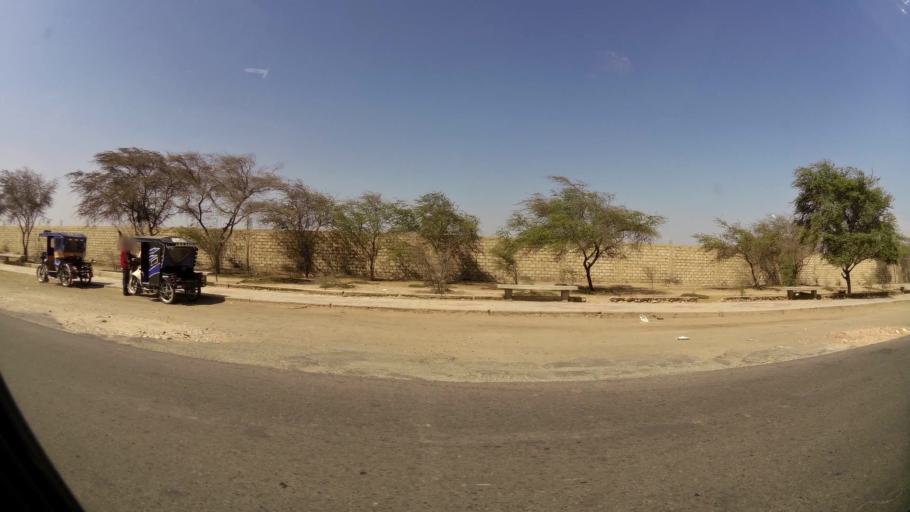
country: PE
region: Lambayeque
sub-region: Provincia de Chiclayo
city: Chiclayo
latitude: -6.7936
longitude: -79.8316
